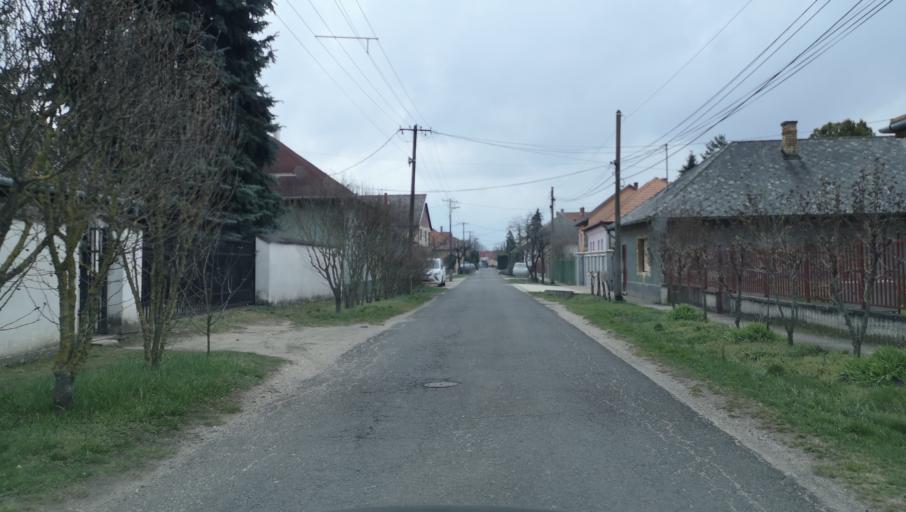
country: HU
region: Pest
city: Monor
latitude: 47.3547
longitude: 19.4465
